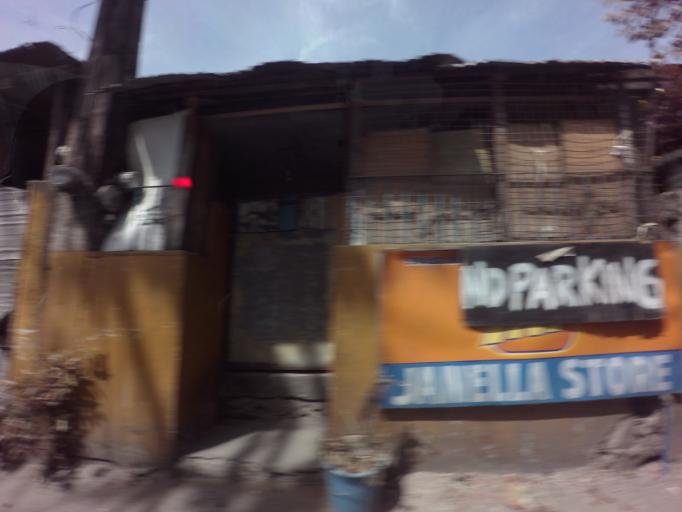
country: PH
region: Calabarzon
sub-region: Province of Rizal
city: Taguig
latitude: 14.5278
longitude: 121.0731
